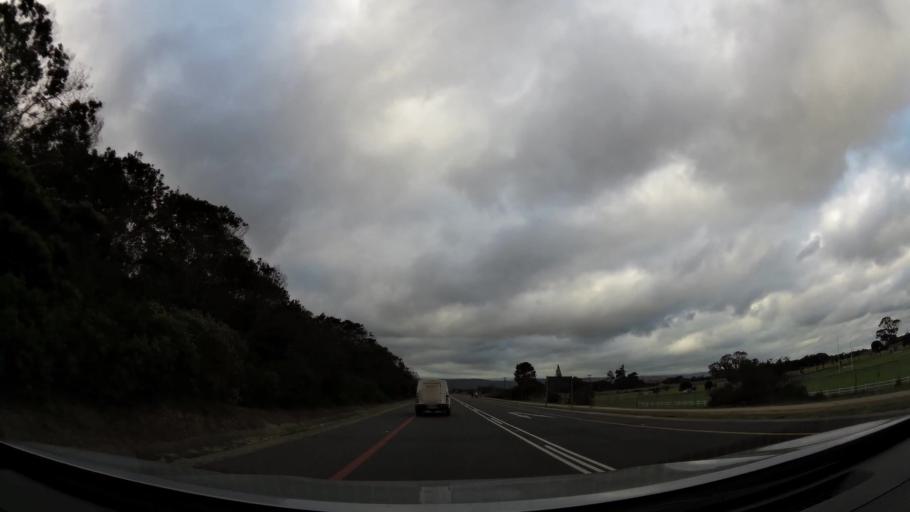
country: ZA
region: Western Cape
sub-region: Eden District Municipality
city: Plettenberg Bay
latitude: -34.0385
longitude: 23.3709
